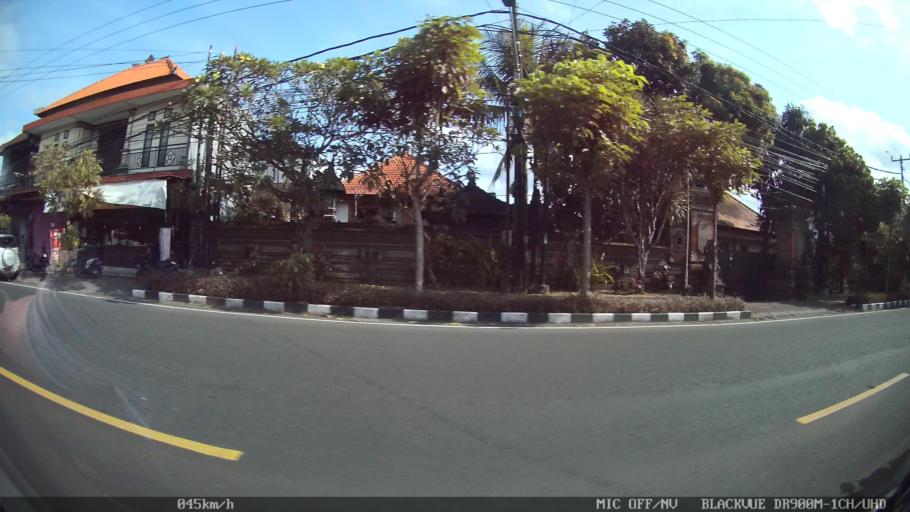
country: ID
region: Bali
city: Banjar Jumbayah
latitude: -8.5639
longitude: 115.1696
